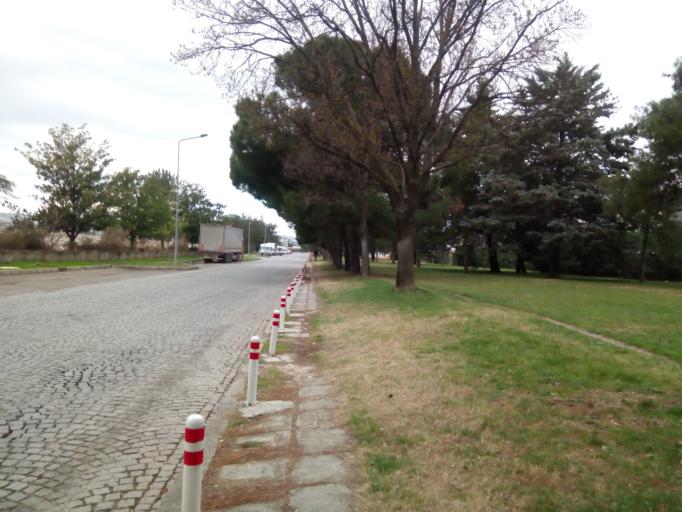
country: TR
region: Bursa
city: Niluefer
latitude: 40.2478
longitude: 28.9603
